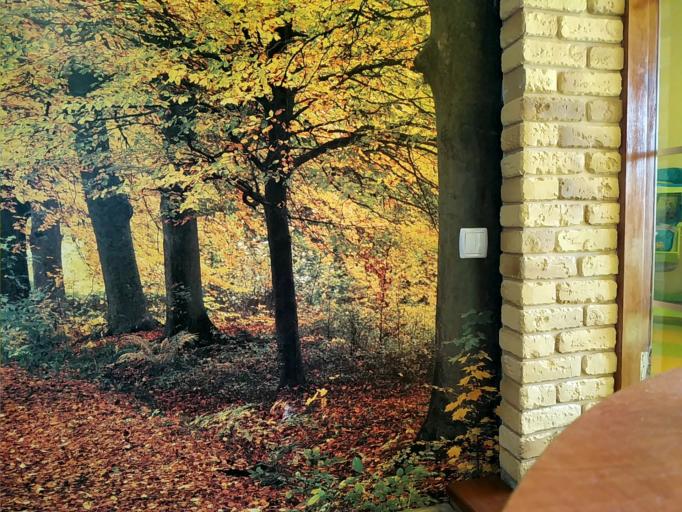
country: RU
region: Novgorod
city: Staraya Russa
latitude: 57.8342
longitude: 31.4782
